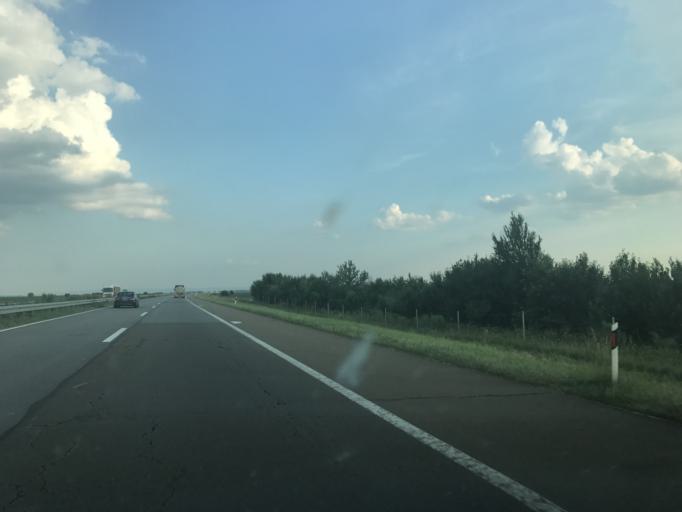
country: RS
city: Zmajevo
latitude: 45.5040
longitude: 19.7269
